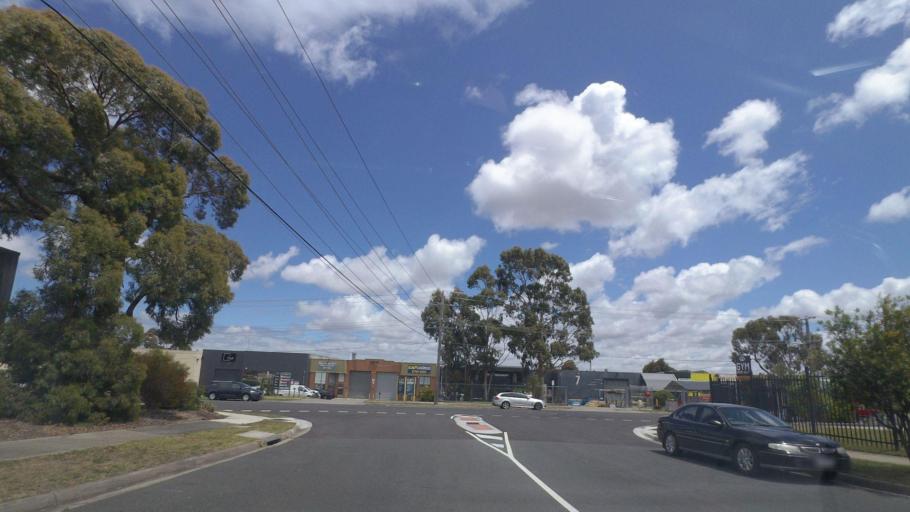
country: AU
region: Victoria
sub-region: Knox
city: Scoresby
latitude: -37.9105
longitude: 145.2448
